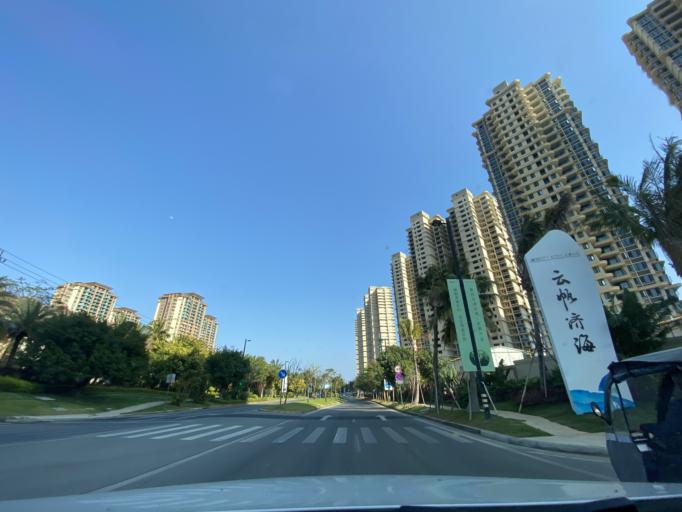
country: CN
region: Hainan
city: Xincun
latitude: 18.4230
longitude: 109.9380
